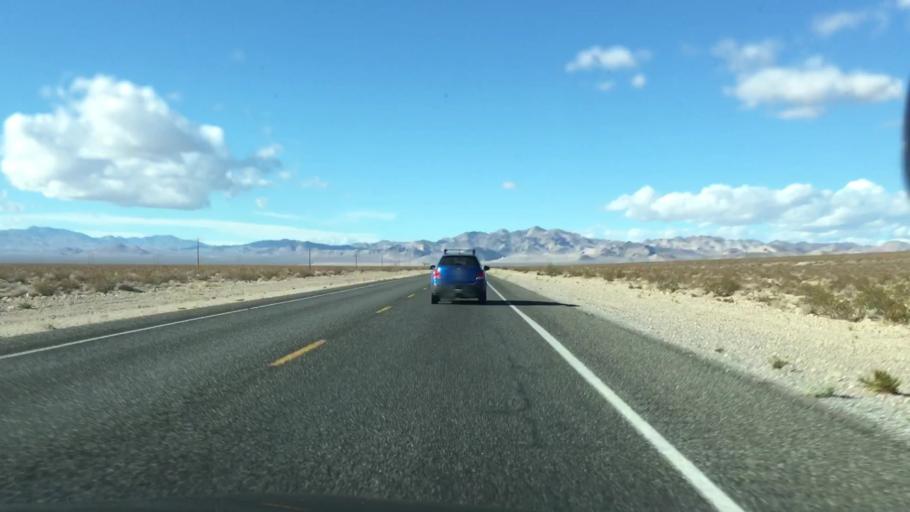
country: US
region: Nevada
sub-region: Nye County
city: Beatty
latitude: 36.8135
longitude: -116.7308
